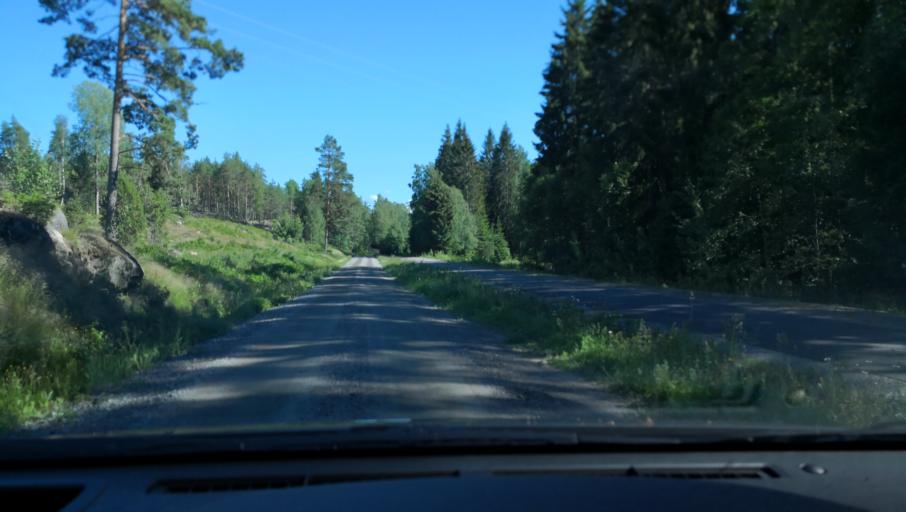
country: SE
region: Soedermanland
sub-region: Eskilstuna Kommun
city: Eskilstuna
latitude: 59.3321
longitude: 16.5784
